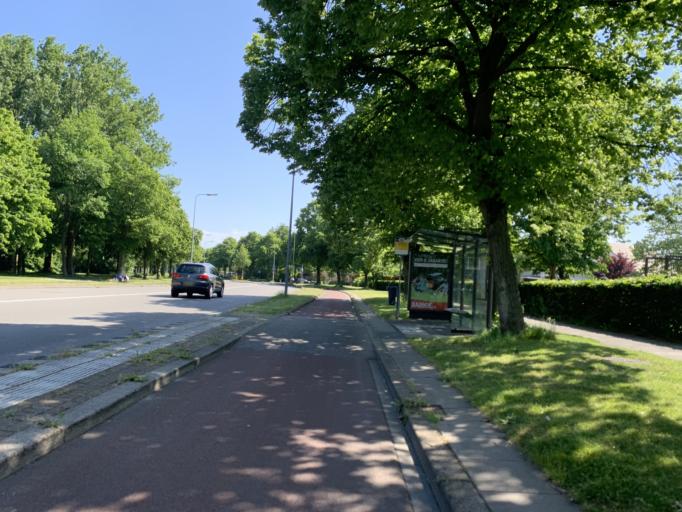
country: NL
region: Groningen
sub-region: Gemeente Groningen
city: Groningen
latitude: 53.2203
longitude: 6.5287
